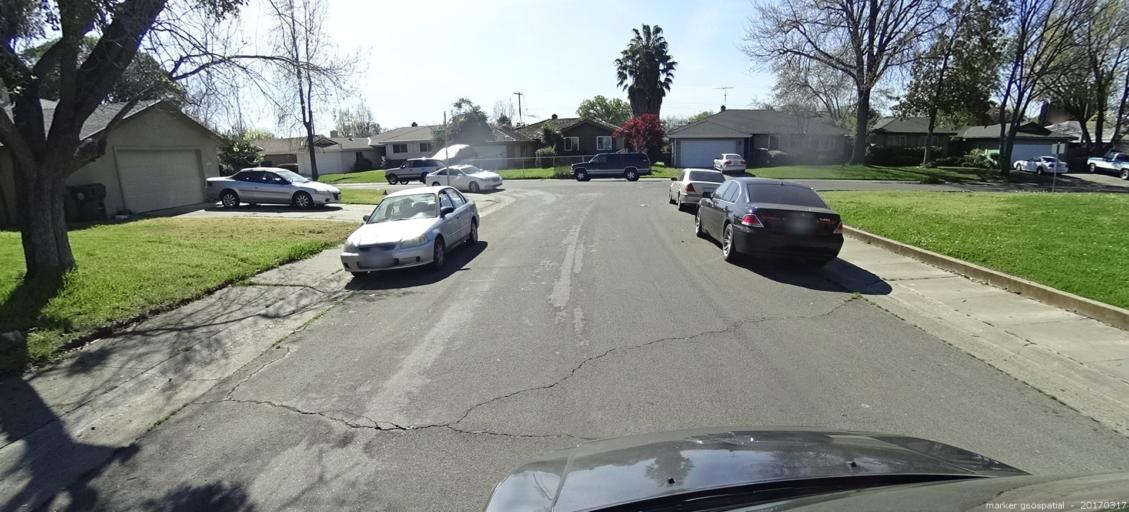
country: US
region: California
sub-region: Sacramento County
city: Parkway
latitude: 38.4908
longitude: -121.4949
